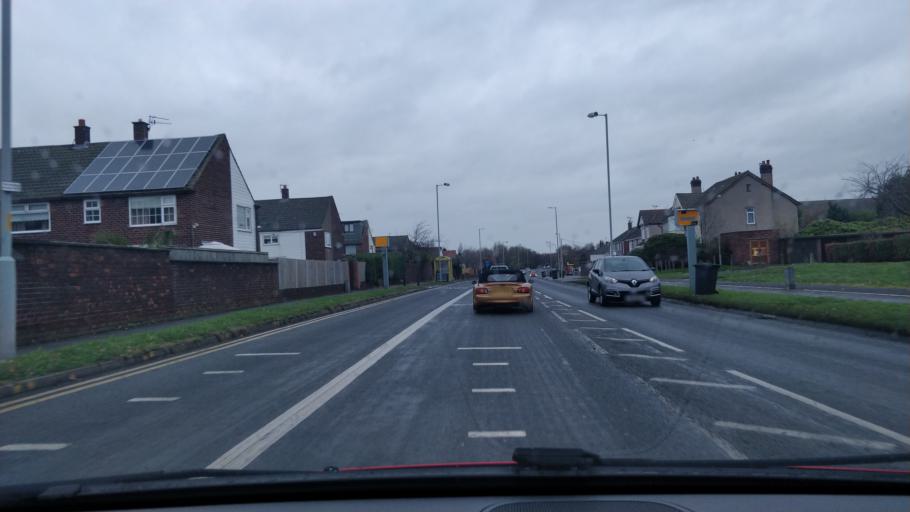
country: GB
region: England
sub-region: Sefton
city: Litherland
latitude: 53.4832
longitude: -2.9957
